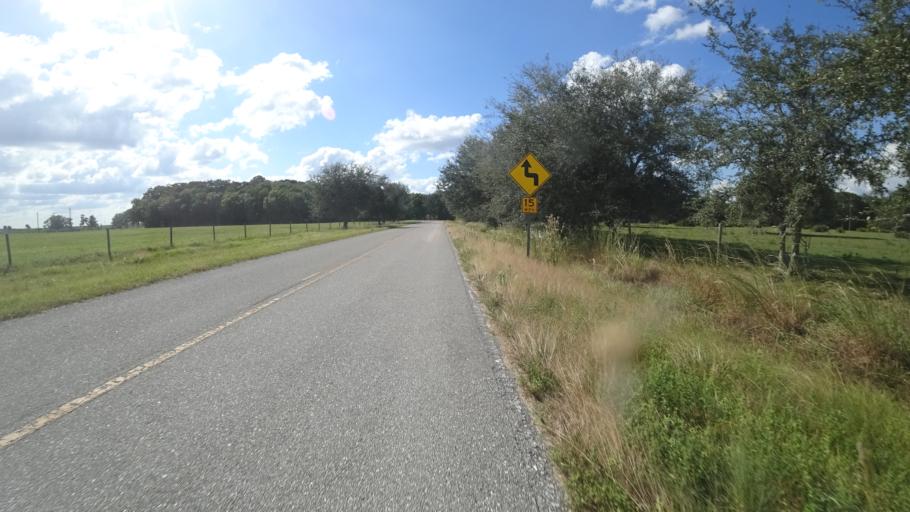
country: US
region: Florida
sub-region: DeSoto County
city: Nocatee
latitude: 27.2733
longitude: -82.0750
